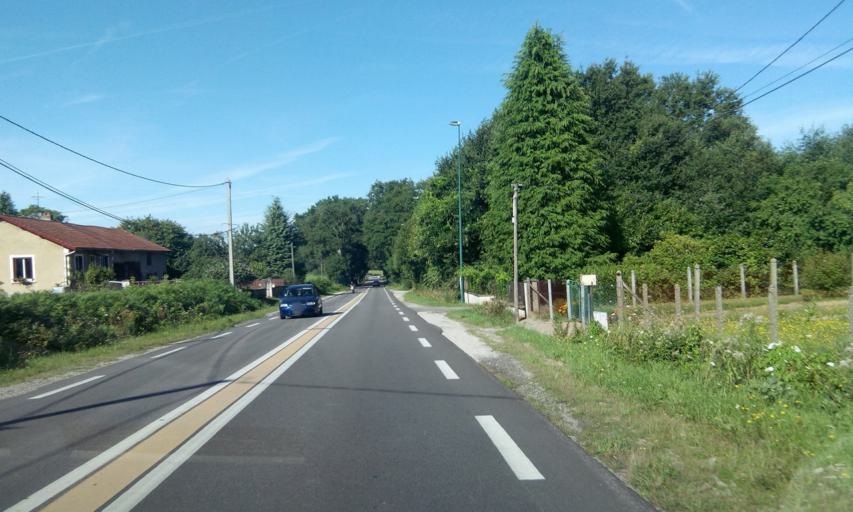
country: FR
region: Limousin
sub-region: Departement de la Haute-Vienne
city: Panazol
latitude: 45.8424
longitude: 1.3330
